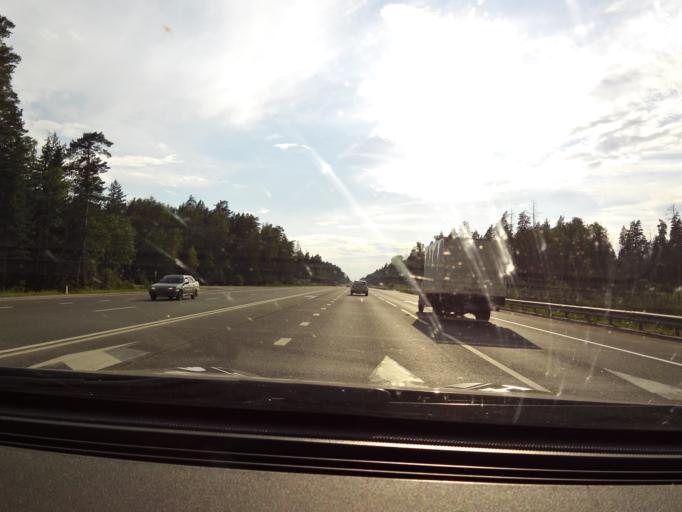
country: RU
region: Vladimir
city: Stepantsevo
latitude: 56.2259
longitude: 41.6325
